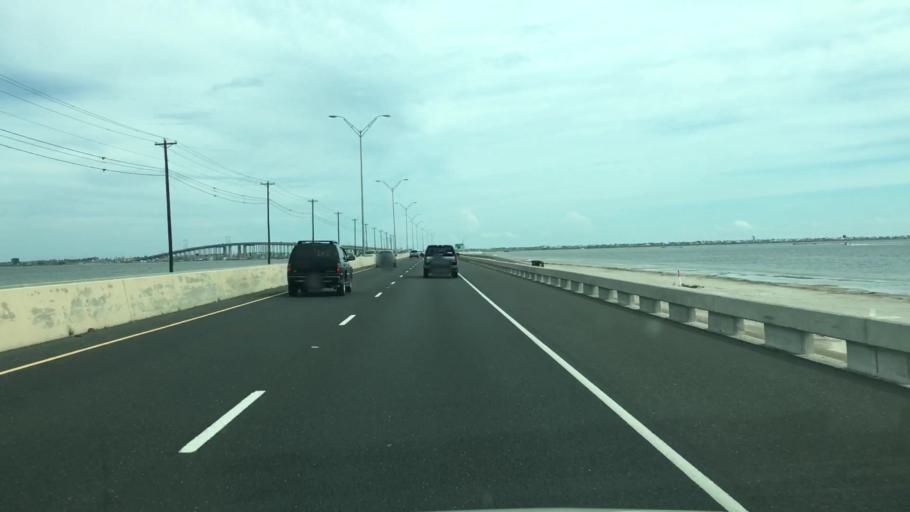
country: US
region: Texas
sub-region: Nueces County
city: Corpus Christi
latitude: 27.6443
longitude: -97.2497
